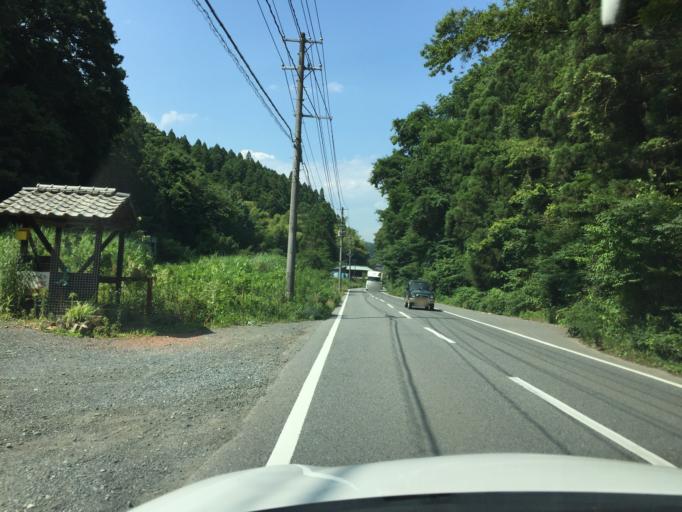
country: JP
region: Ibaraki
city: Kitaibaraki
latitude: 36.9154
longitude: 140.7446
